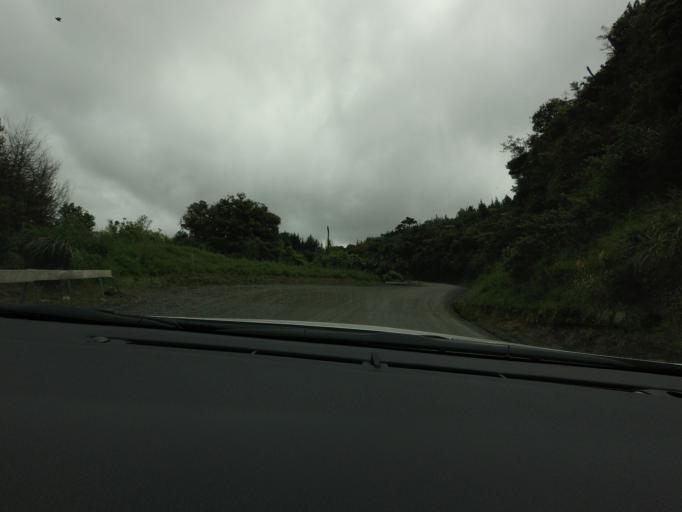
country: NZ
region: Auckland
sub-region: Auckland
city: Warkworth
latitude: -36.4839
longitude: 174.6057
